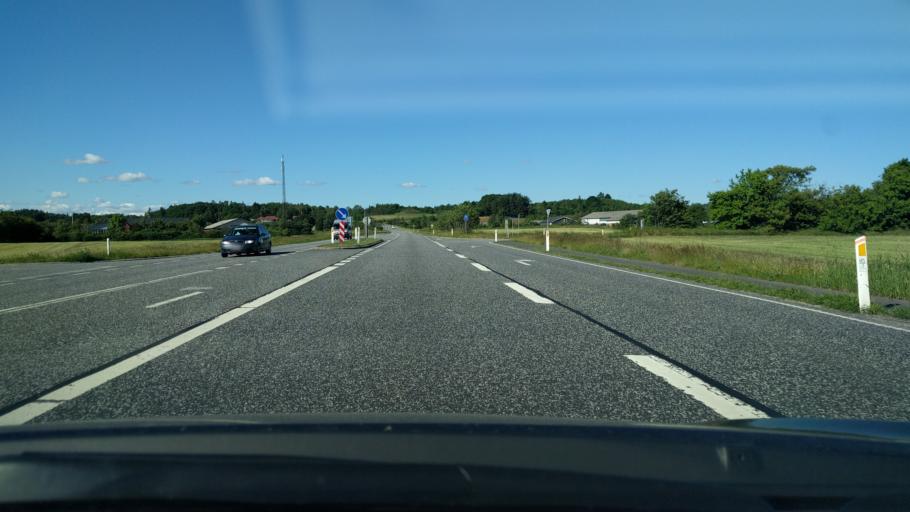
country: DK
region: North Denmark
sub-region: Vesthimmerland Kommune
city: Alestrup
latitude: 56.5756
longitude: 9.4955
